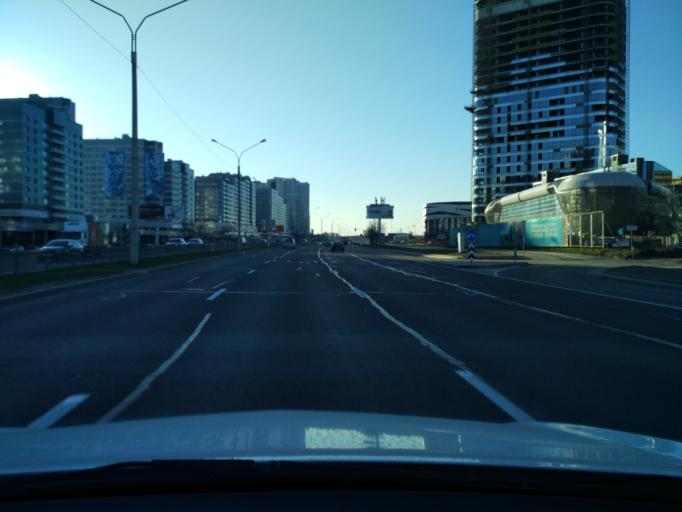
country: BY
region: Minsk
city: Zhdanovichy
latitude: 53.9393
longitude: 27.4727
